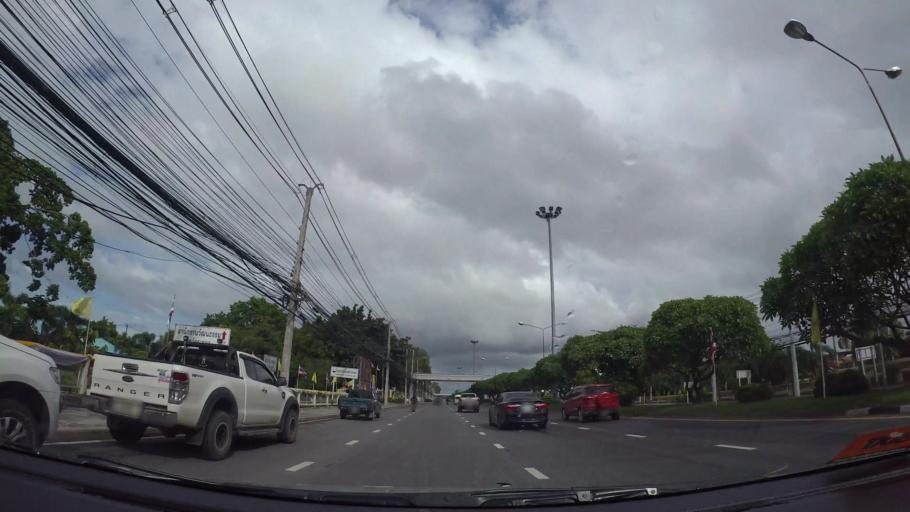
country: TH
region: Rayong
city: Rayong
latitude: 12.6832
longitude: 101.2366
